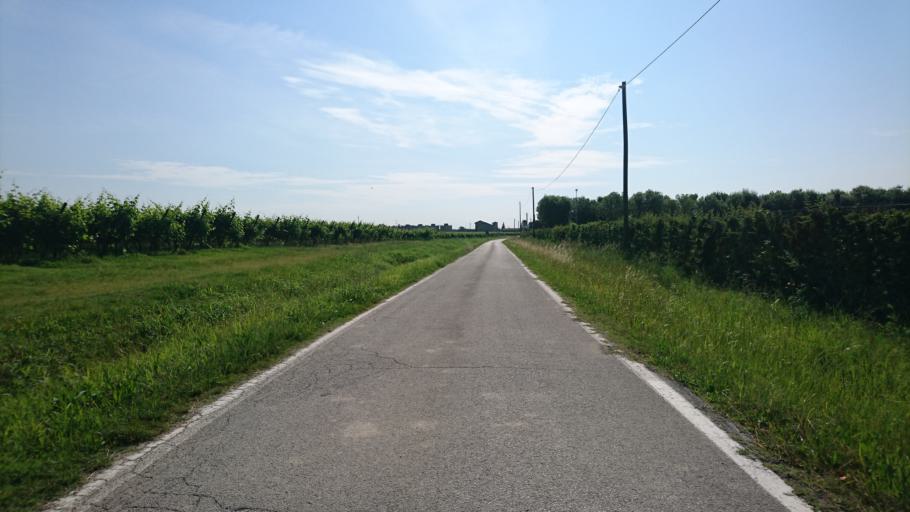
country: IT
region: Veneto
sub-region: Provincia di Padova
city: Merlara
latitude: 45.1749
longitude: 11.4349
